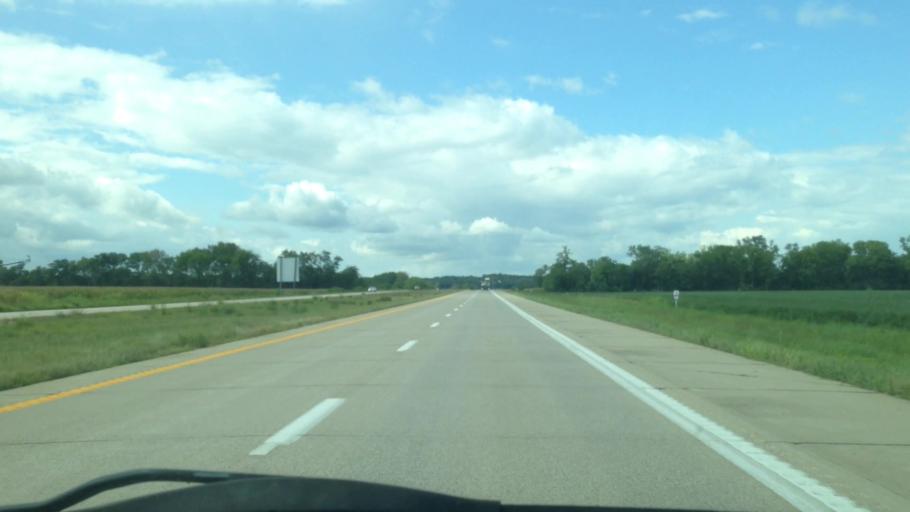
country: US
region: Missouri
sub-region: Clark County
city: Kahoka
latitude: 40.4127
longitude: -91.5723
